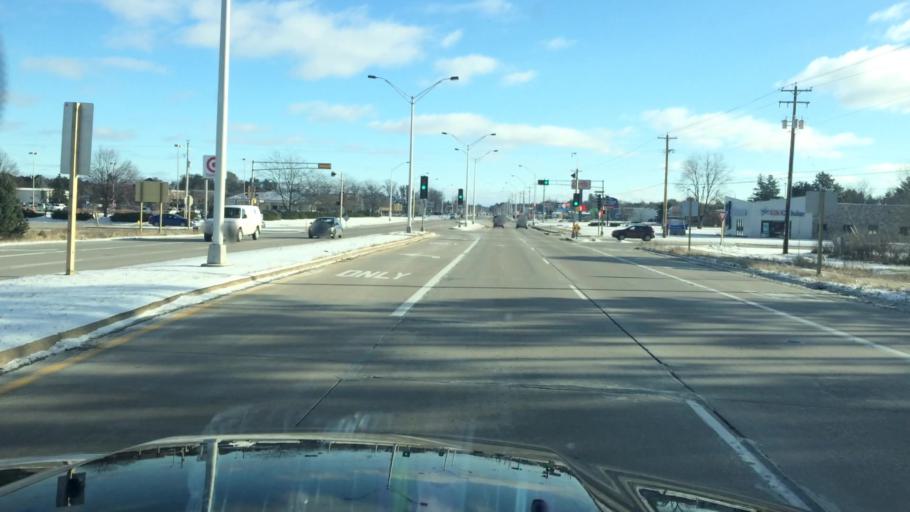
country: US
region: Wisconsin
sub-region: Portage County
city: Whiting
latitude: 44.5233
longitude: -89.5252
